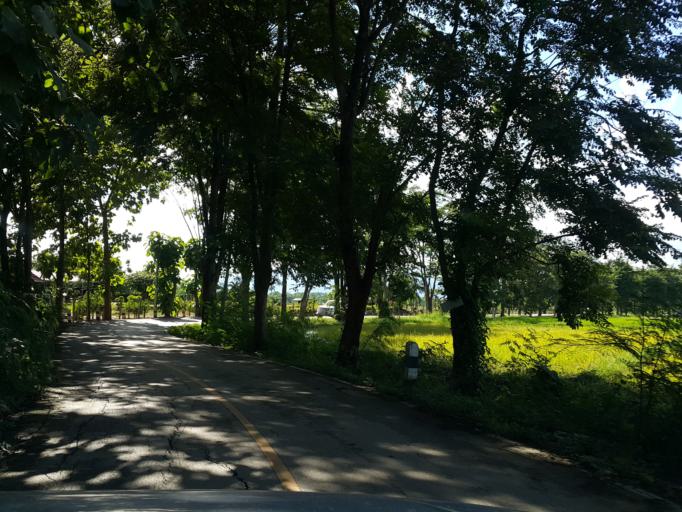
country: TH
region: Chiang Mai
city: San Kamphaeng
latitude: 18.7981
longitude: 99.1336
